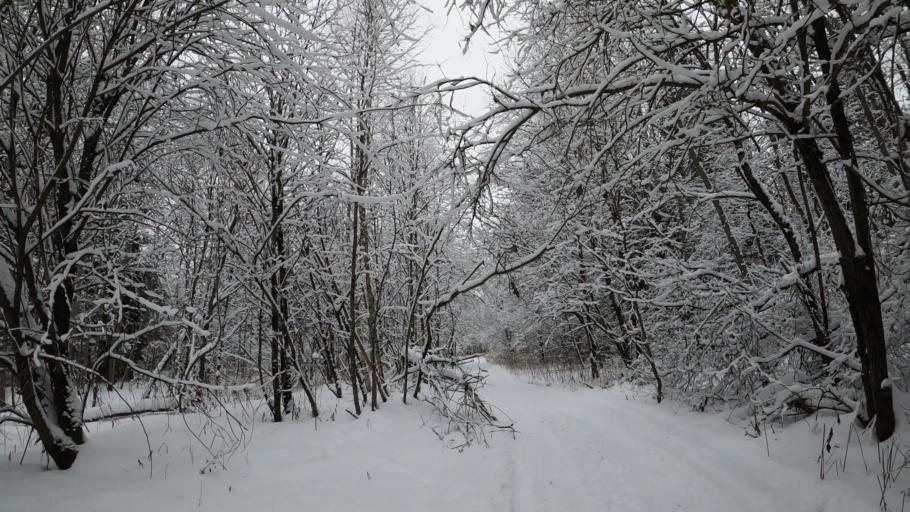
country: RU
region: Moskovskaya
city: Firsanovka
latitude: 55.9361
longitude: 37.2180
